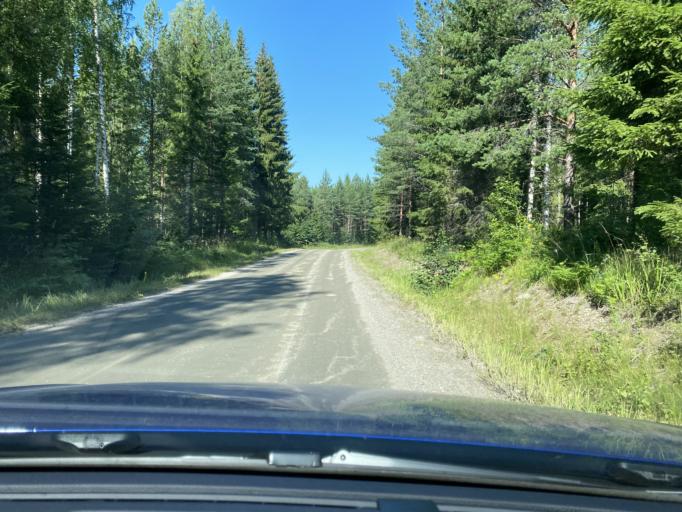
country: FI
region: Central Finland
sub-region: Jyvaeskylae
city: Korpilahti
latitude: 61.8732
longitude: 25.4149
